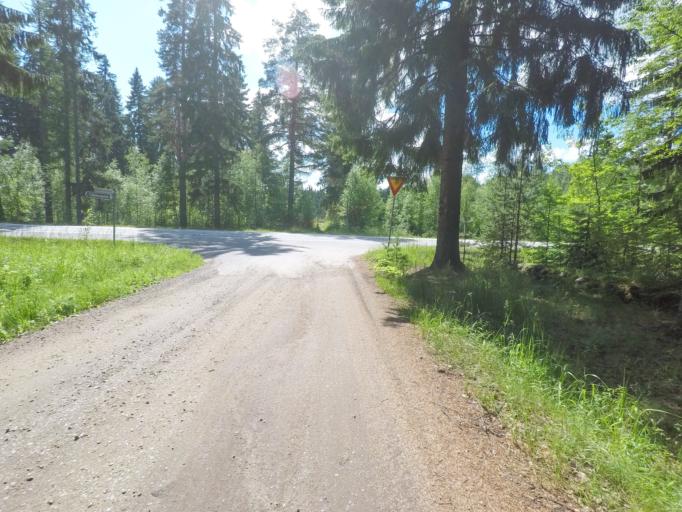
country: FI
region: Southern Savonia
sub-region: Savonlinna
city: Punkaharju
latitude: 61.8036
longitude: 29.3176
